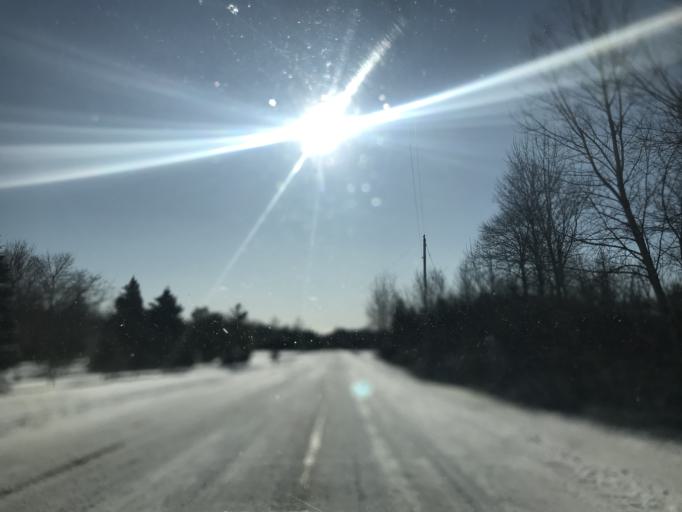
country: US
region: Wisconsin
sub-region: Door County
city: Sturgeon Bay
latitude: 44.8284
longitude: -87.5041
